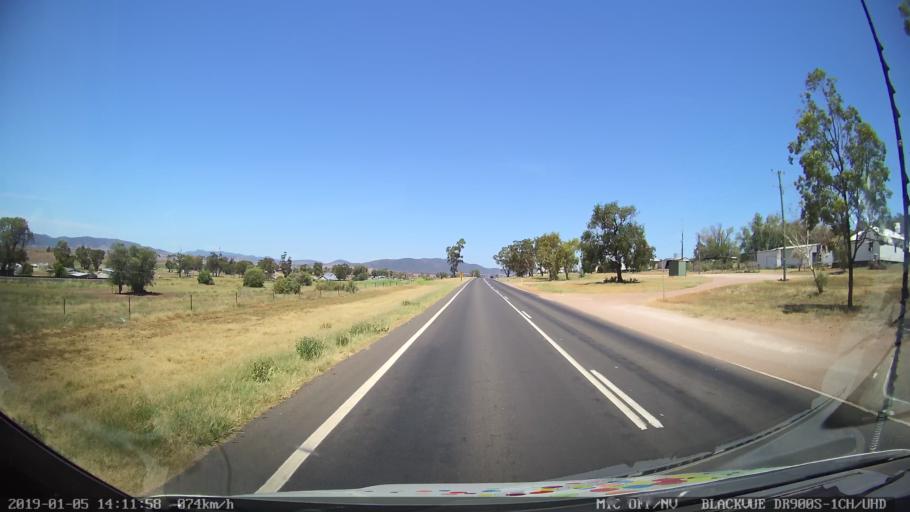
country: AU
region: New South Wales
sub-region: Gunnedah
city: Gunnedah
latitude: -31.2468
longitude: 150.4643
